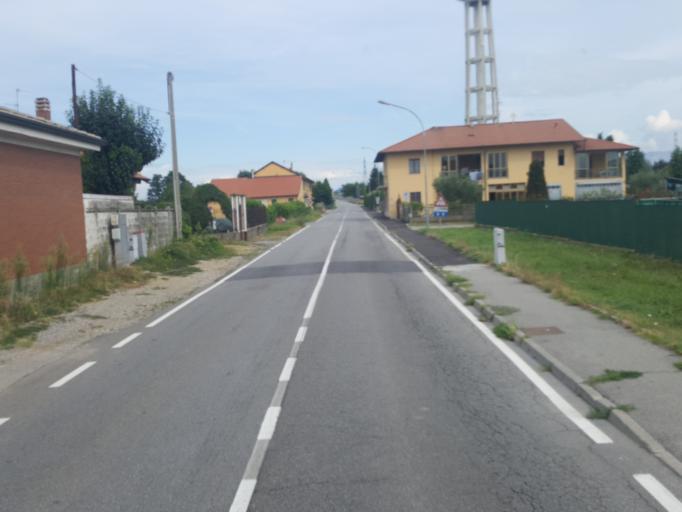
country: IT
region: Lombardy
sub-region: Citta metropolitana di Milano
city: Basiano
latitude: 45.5831
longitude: 9.4616
